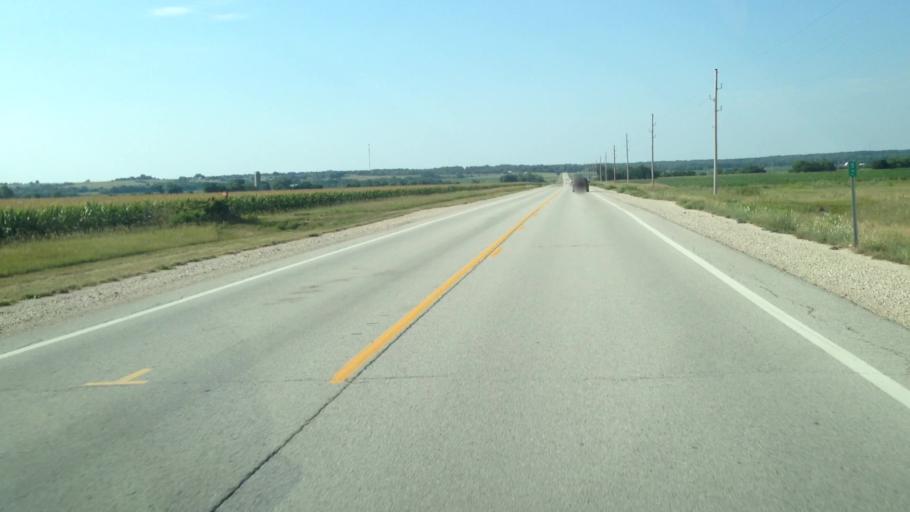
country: US
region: Kansas
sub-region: Anderson County
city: Garnett
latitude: 38.0552
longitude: -95.1694
